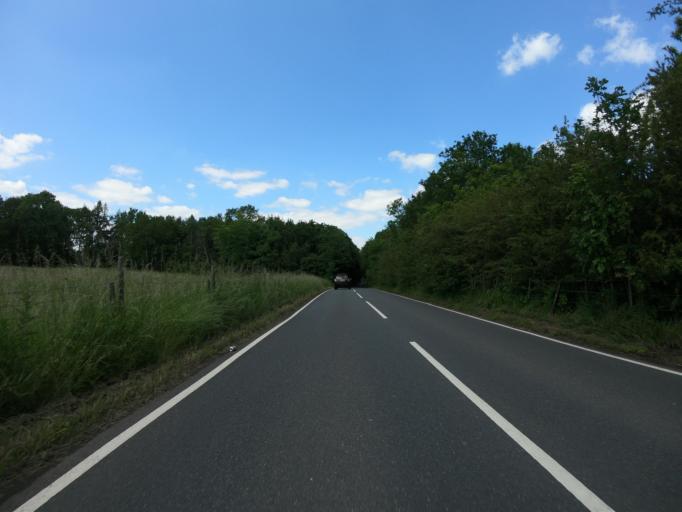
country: GB
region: England
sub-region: Kent
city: Halstead
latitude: 51.3120
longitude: 0.1356
